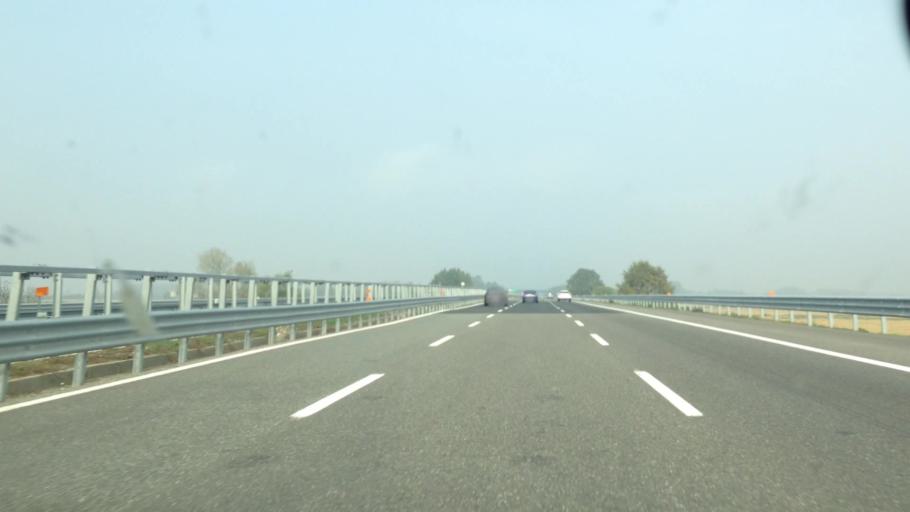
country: IT
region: Piedmont
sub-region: Provincia di Alessandria
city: Borgo San Martino
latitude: 45.0846
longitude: 8.5055
